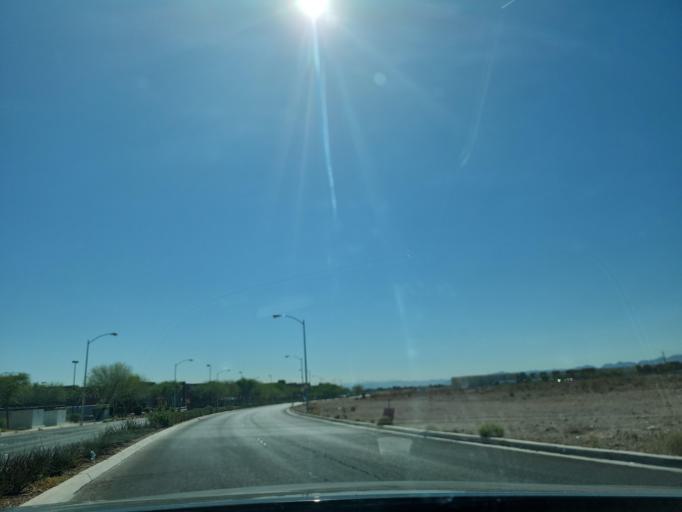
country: US
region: Nevada
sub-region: Clark County
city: Enterprise
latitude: 36.0611
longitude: -115.2524
